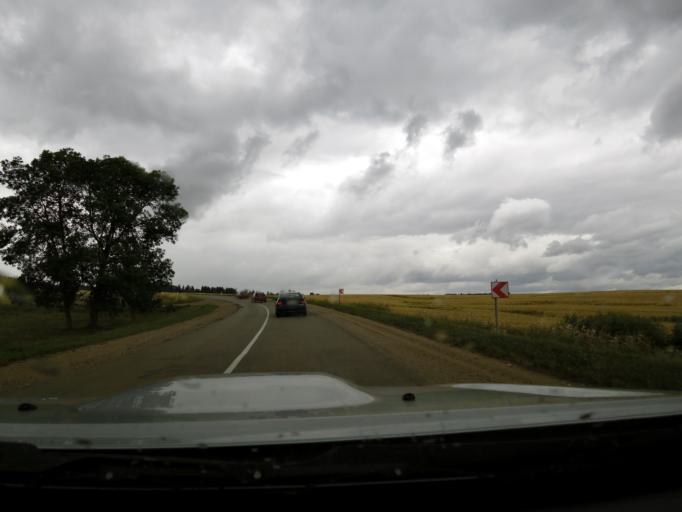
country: LT
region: Vilnius County
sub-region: Vilnius
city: Fabijoniskes
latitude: 55.0063
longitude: 25.2531
